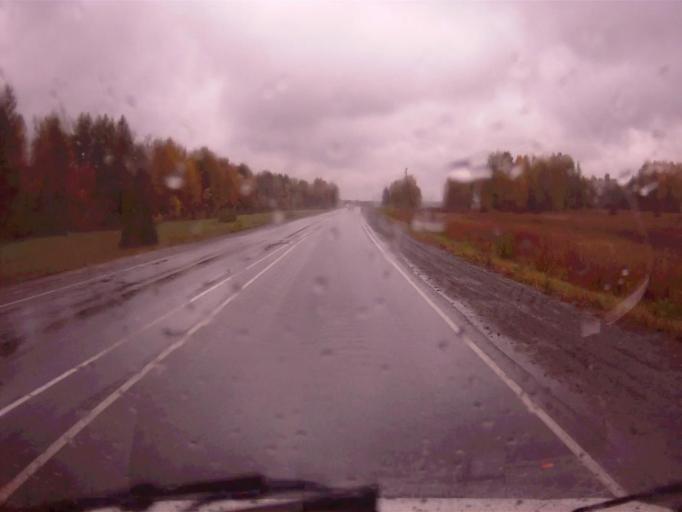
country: RU
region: Chelyabinsk
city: Roshchino
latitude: 55.4005
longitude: 61.0734
